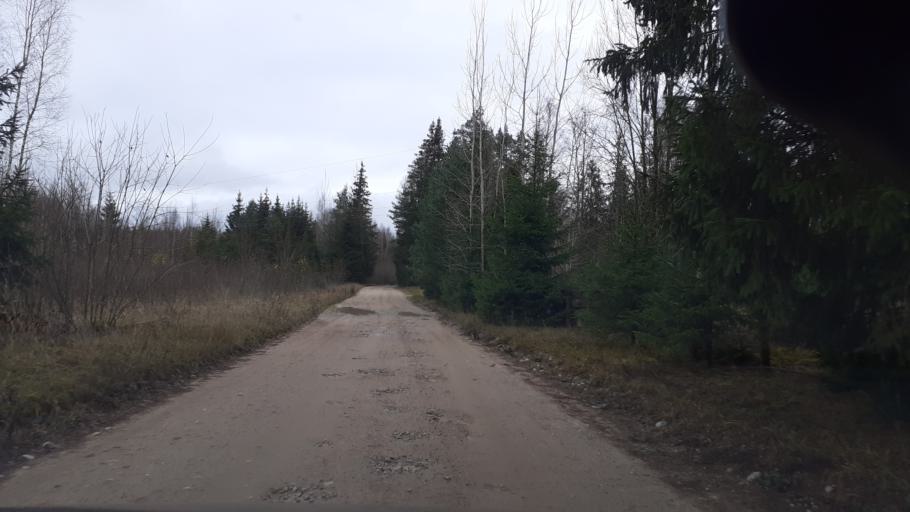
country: LV
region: Kuldigas Rajons
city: Kuldiga
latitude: 57.0268
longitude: 21.8695
